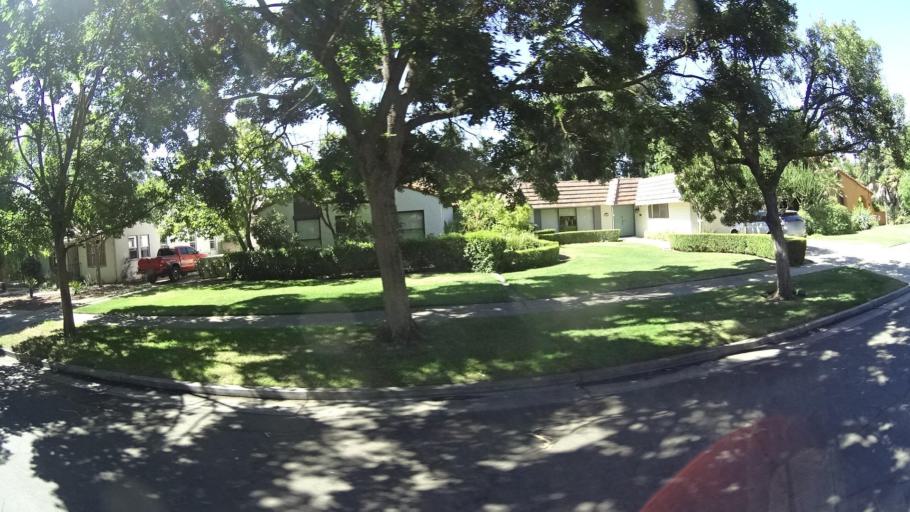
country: US
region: California
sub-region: Fresno County
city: Fresno
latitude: 36.7731
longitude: -119.8072
